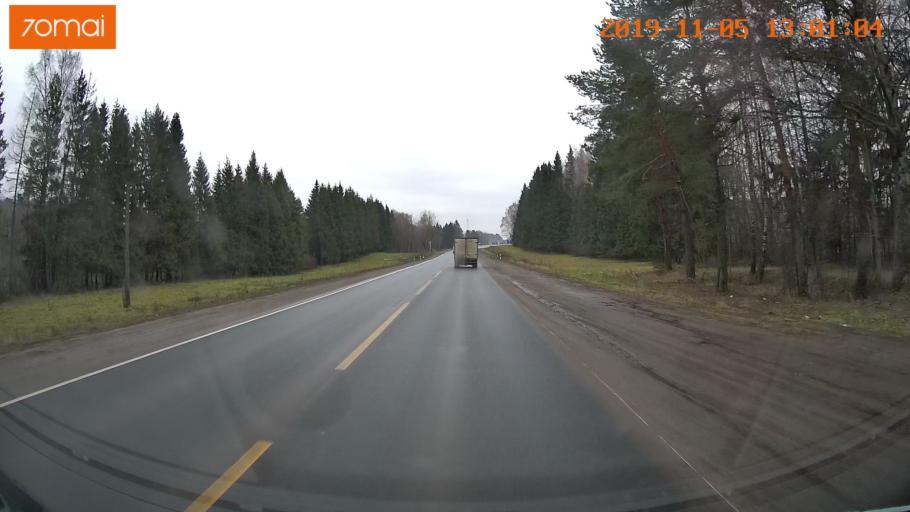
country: RU
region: Ivanovo
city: Kokhma
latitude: 56.9107
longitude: 41.1564
